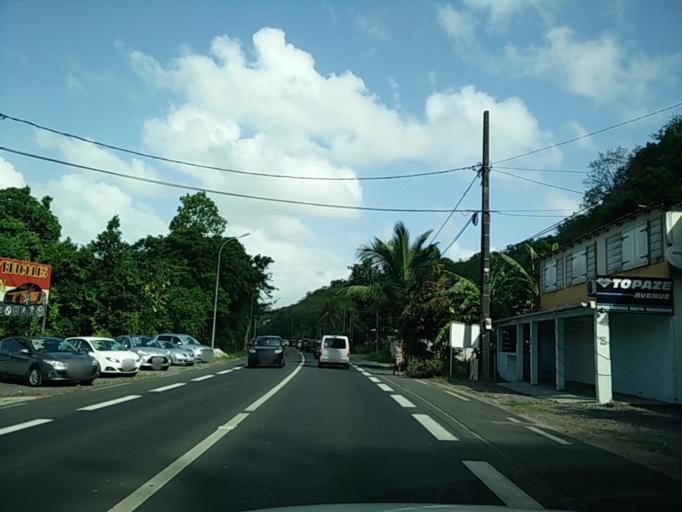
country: GP
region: Guadeloupe
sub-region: Guadeloupe
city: Le Gosier
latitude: 16.2166
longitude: -61.4808
